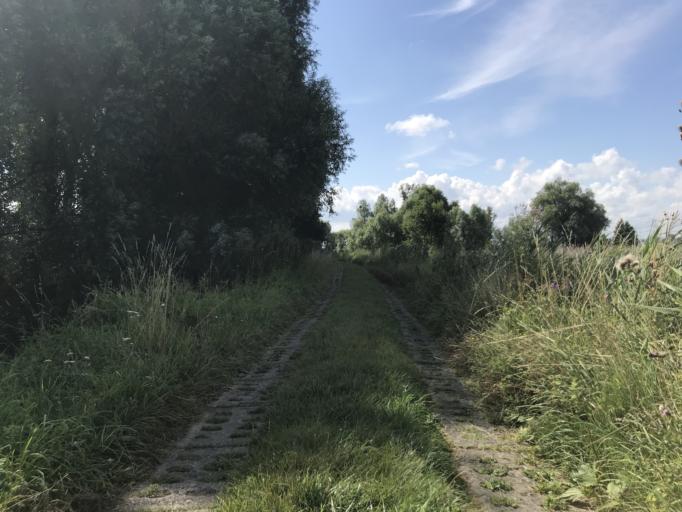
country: PL
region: Pomeranian Voivodeship
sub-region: Gdansk
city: Gdansk
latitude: 54.3213
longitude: 18.6722
